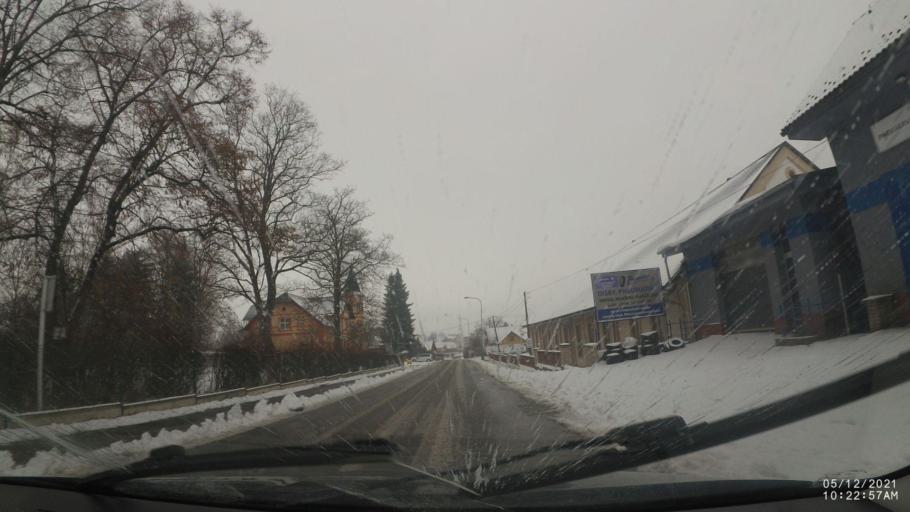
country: CZ
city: Vamberk
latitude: 50.1138
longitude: 16.2906
